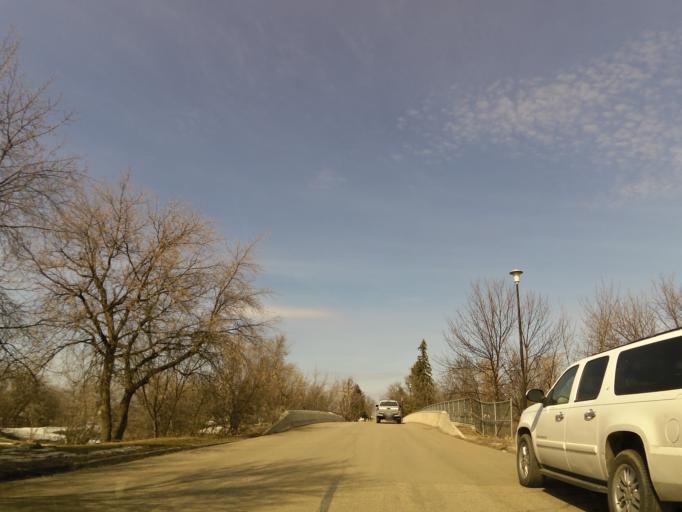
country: US
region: North Dakota
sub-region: Walsh County
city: Grafton
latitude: 48.4228
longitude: -97.4086
